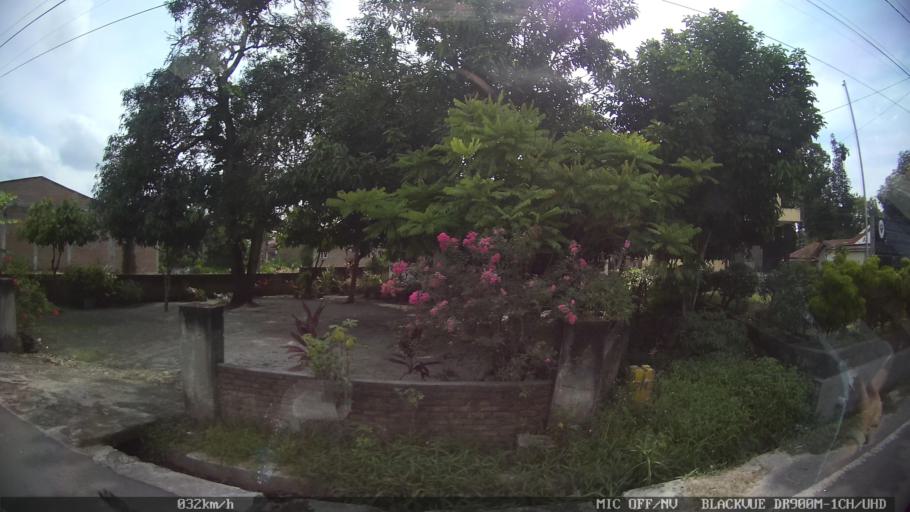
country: ID
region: North Sumatra
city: Percut
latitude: 3.6018
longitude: 98.8579
